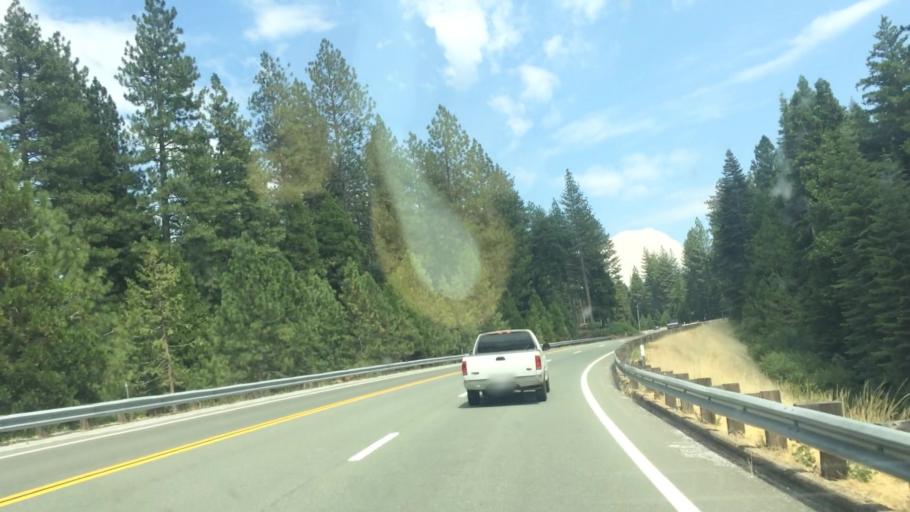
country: US
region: California
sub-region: Amador County
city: Pioneer
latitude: 38.5145
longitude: -120.4816
